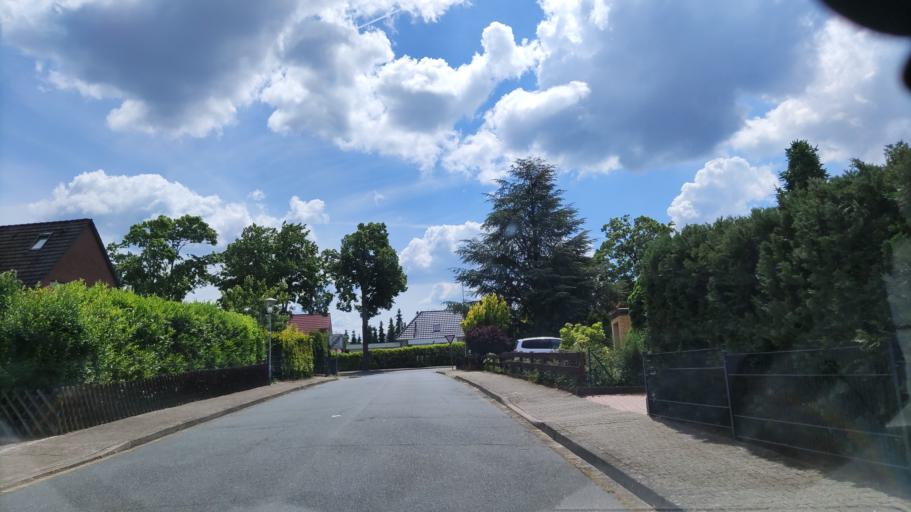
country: DE
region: Lower Saxony
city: Deutsch Evern
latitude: 53.2050
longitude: 10.4436
